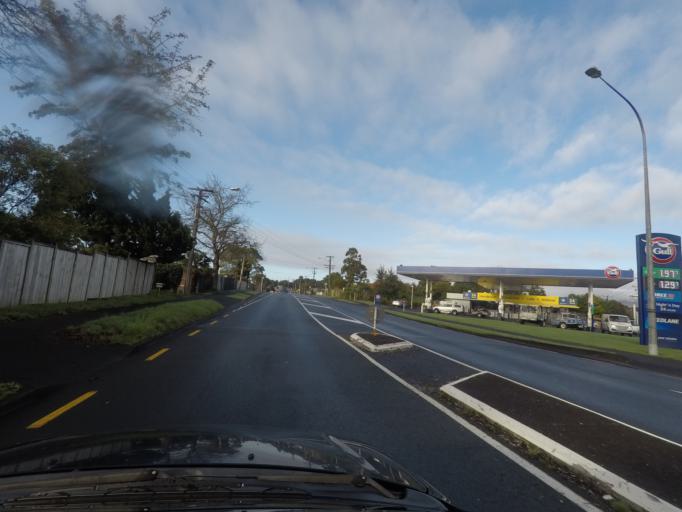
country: NZ
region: Auckland
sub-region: Auckland
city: Waitakere
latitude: -36.8937
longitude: 174.6199
